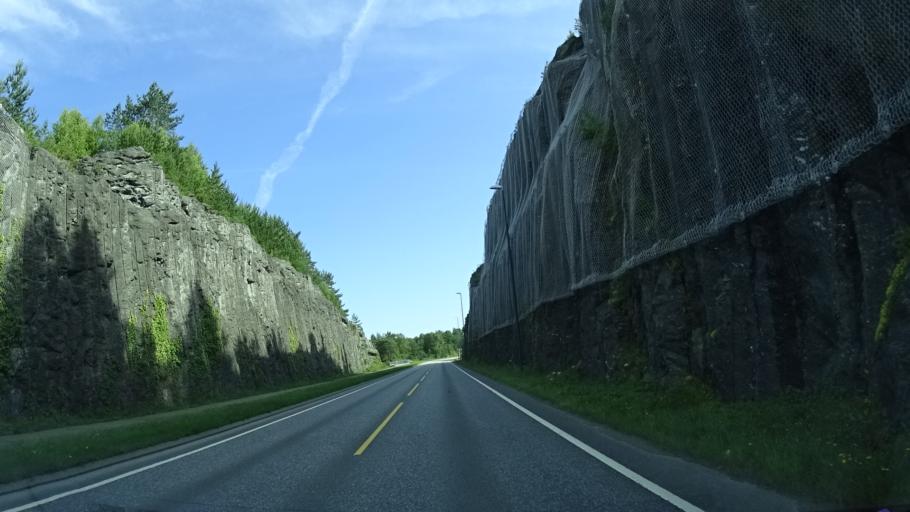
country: NO
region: Hordaland
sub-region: Bomlo
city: Mosterhamn
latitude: 59.7337
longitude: 5.3617
